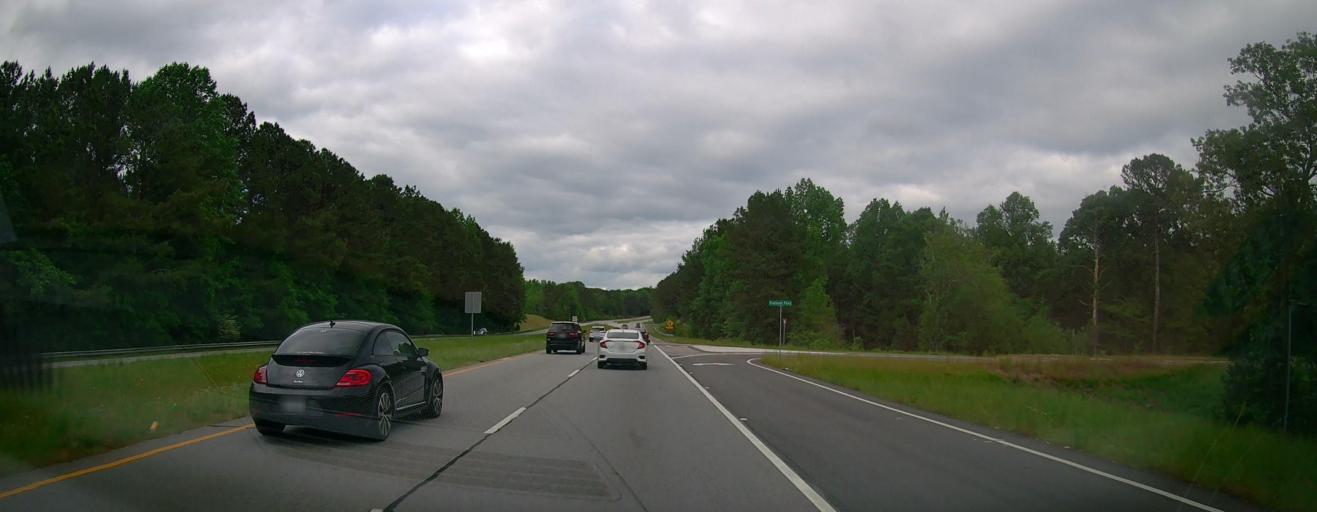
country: US
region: Georgia
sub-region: Walton County
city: Monroe
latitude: 33.8171
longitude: -83.6757
